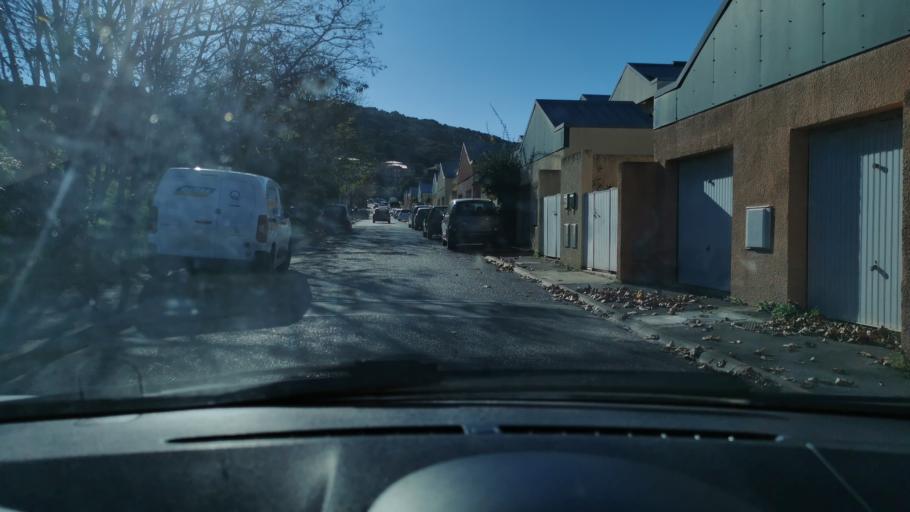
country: FR
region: Languedoc-Roussillon
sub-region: Departement de l'Herault
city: Sete
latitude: 43.4102
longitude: 3.6686
